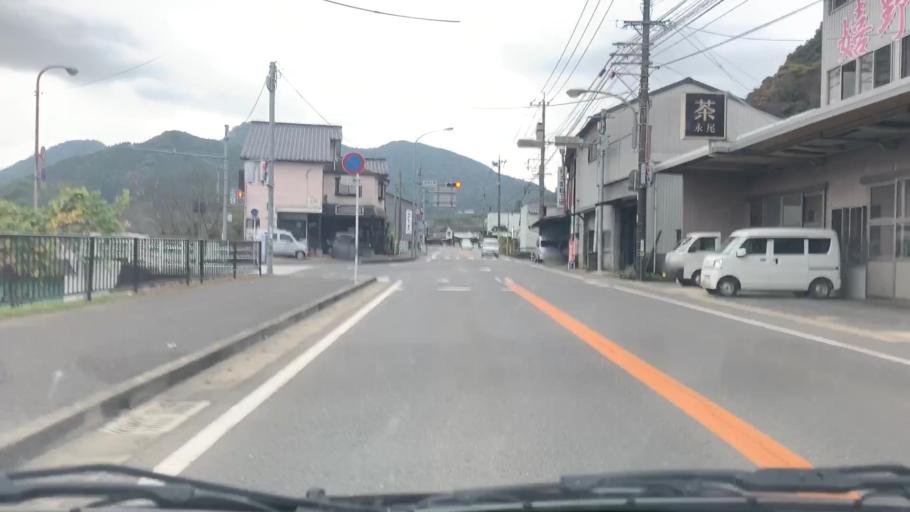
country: JP
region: Saga Prefecture
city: Ureshinomachi-shimojuku
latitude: 33.0922
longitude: 129.9763
